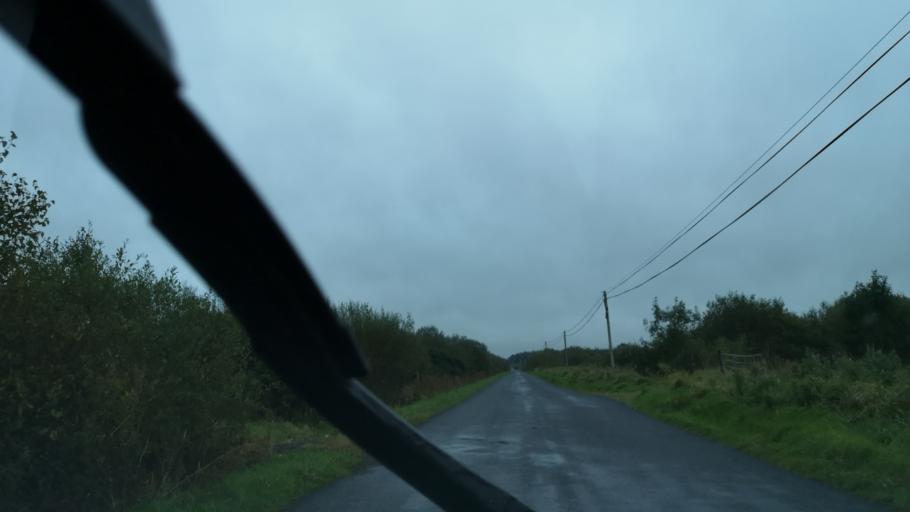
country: IE
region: Connaught
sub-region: Roscommon
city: Ballaghaderreen
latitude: 53.8923
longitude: -8.5733
